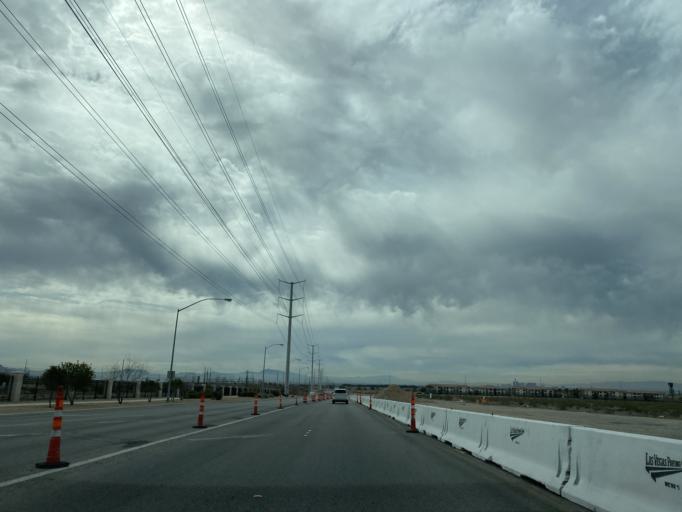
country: US
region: Nevada
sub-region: Clark County
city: Nellis Air Force Base
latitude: 36.2857
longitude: -115.0987
